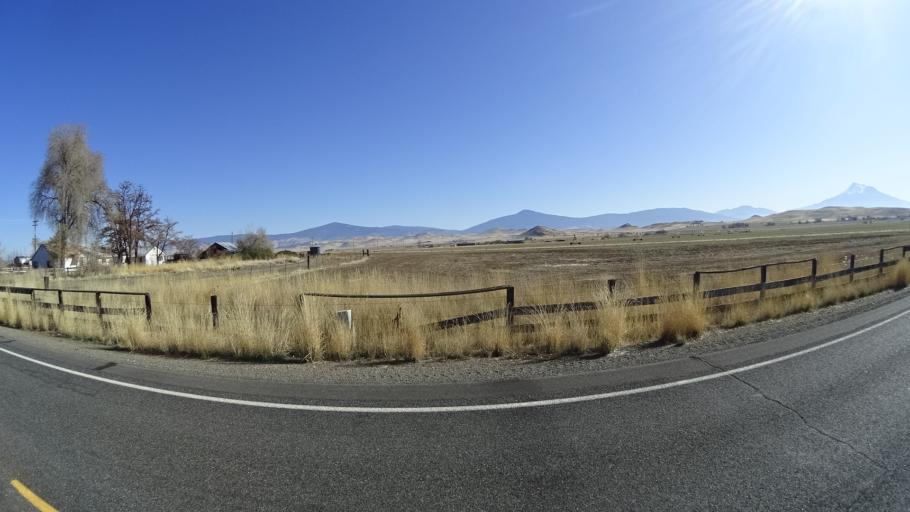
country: US
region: California
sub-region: Siskiyou County
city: Montague
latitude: 41.7558
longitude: -122.5247
